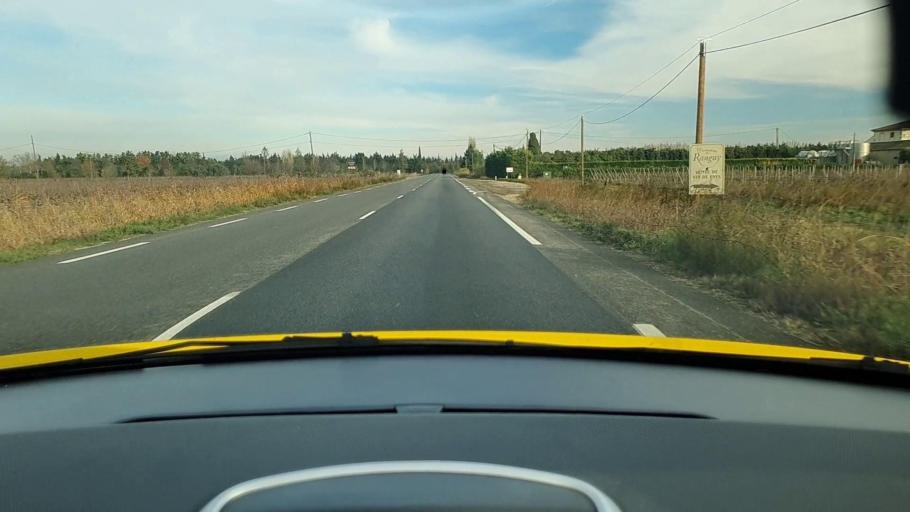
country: FR
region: Languedoc-Roussillon
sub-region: Departement du Gard
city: Beaucaire
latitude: 43.7618
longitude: 4.6168
